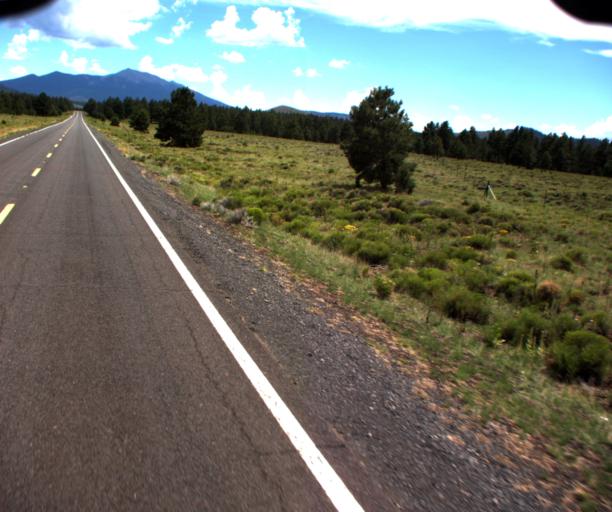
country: US
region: Arizona
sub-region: Coconino County
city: Parks
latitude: 35.4751
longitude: -111.7943
